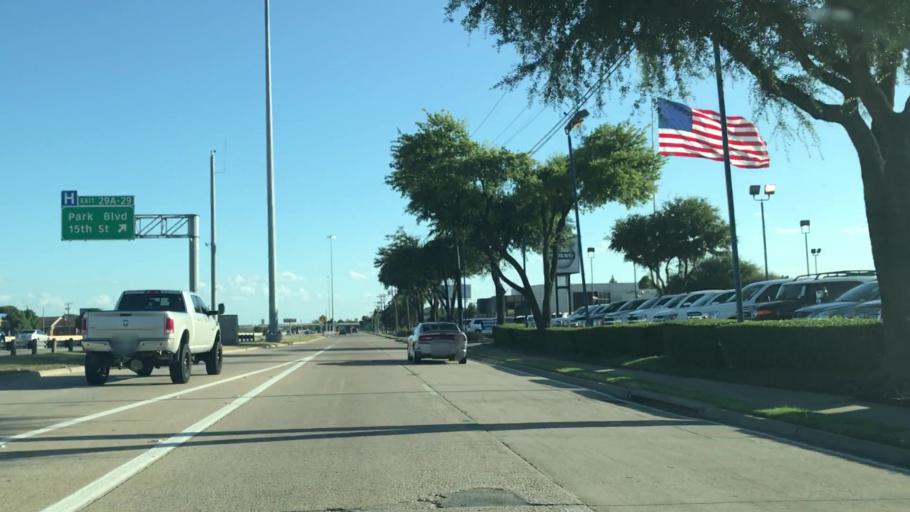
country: US
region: Texas
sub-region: Collin County
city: Plano
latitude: 33.0351
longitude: -96.7062
